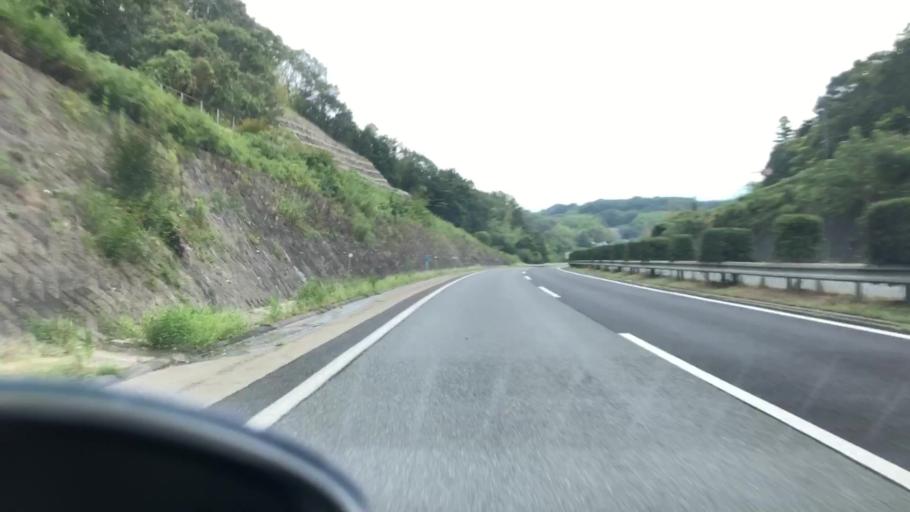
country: JP
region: Hyogo
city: Yashiro
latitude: 34.8913
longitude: 135.0922
